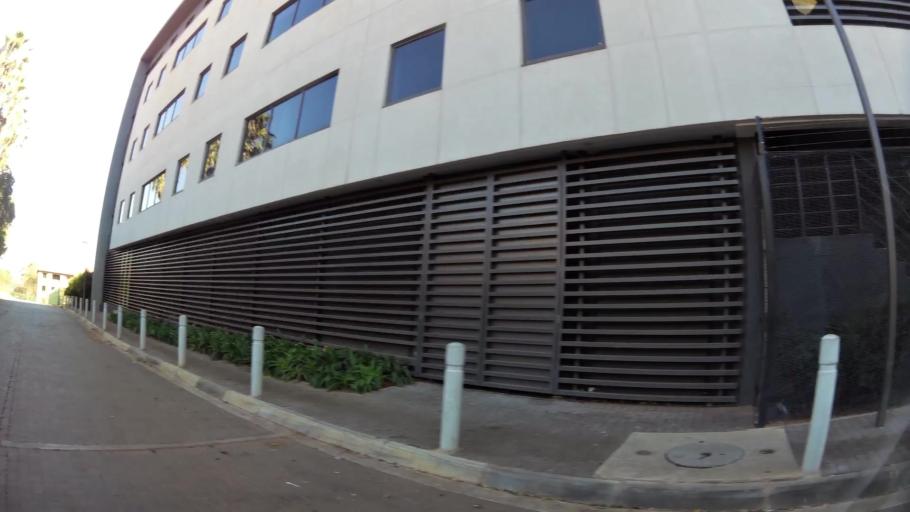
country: ZA
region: Gauteng
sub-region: City of Johannesburg Metropolitan Municipality
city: Johannesburg
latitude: -26.1864
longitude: 28.0395
